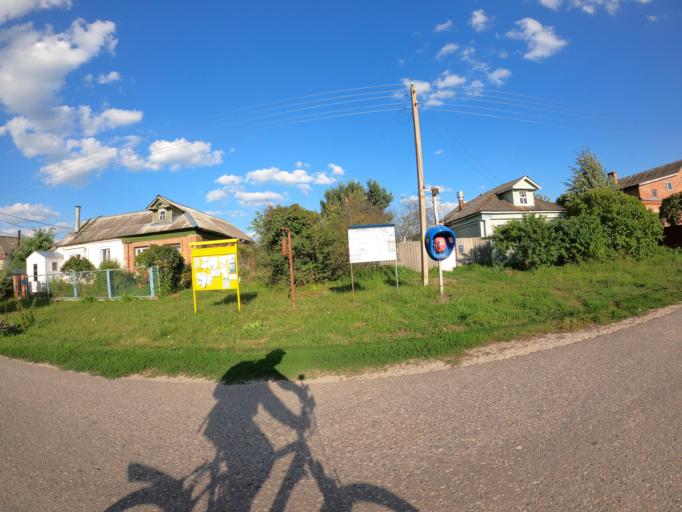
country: RU
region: Moskovskaya
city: Raduzhnyy
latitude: 55.1506
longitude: 38.7367
